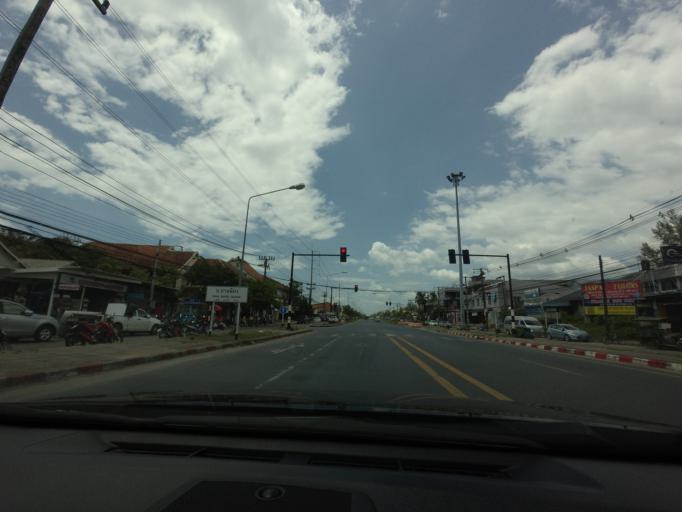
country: TH
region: Phangnga
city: Ban Khao Lak
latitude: 8.6674
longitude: 98.2531
